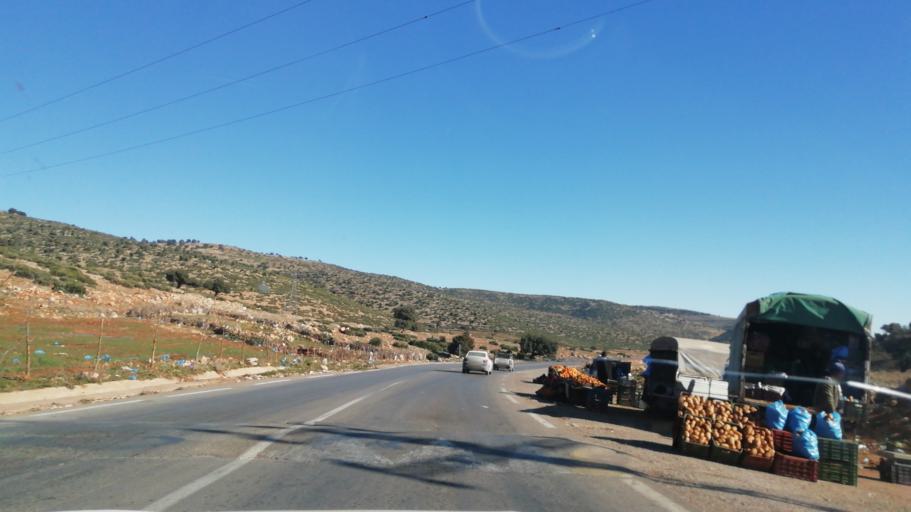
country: DZ
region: Tlemcen
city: Sebdou
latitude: 34.7162
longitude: -1.3319
